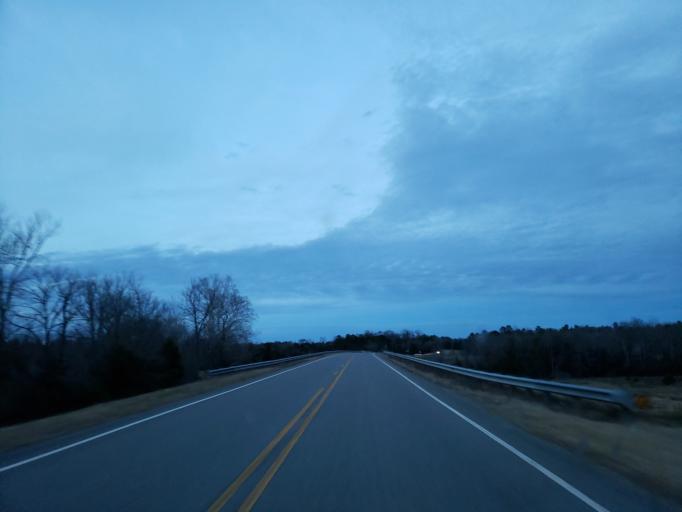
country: US
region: Alabama
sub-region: Greene County
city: Eutaw
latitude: 32.8567
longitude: -88.1007
